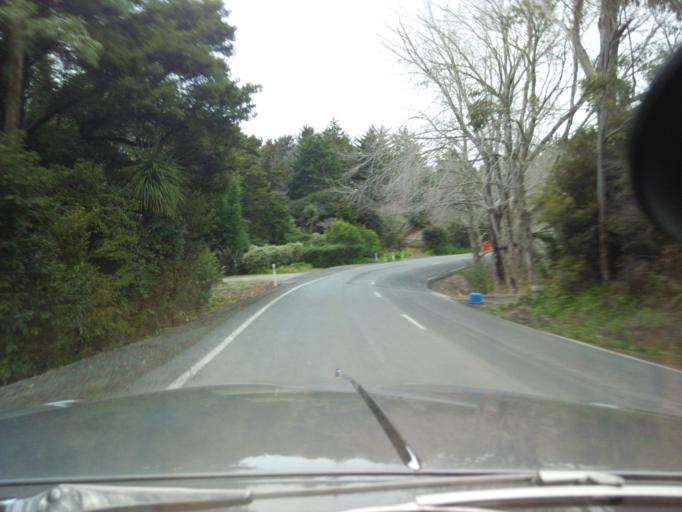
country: NZ
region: Auckland
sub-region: Auckland
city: Warkworth
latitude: -36.5067
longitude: 174.6510
